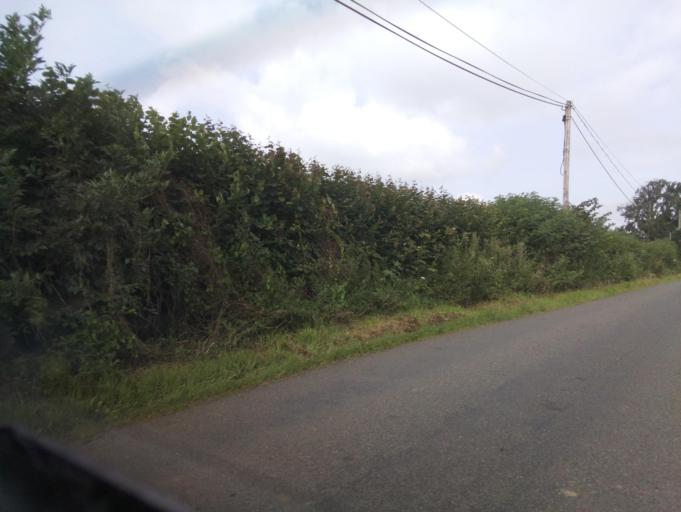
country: GB
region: England
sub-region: Bath and North East Somerset
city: East Harptree
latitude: 51.2670
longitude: -2.5819
